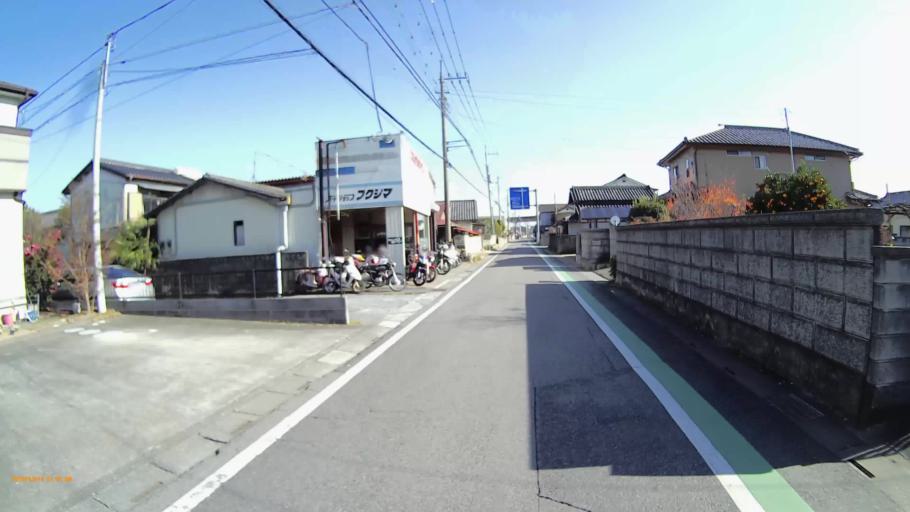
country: JP
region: Saitama
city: Kumagaya
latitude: 36.1225
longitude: 139.4089
